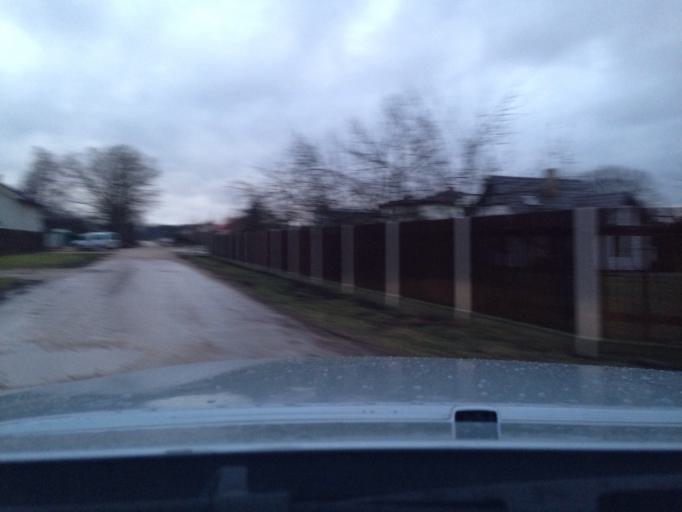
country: LV
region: Marupe
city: Marupe
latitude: 56.9151
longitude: 24.0270
